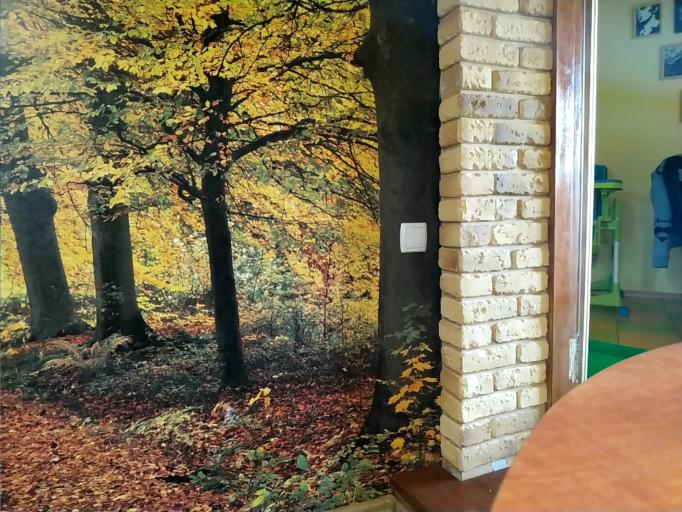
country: RU
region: Leningrad
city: Luga
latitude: 58.9672
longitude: 29.5599
